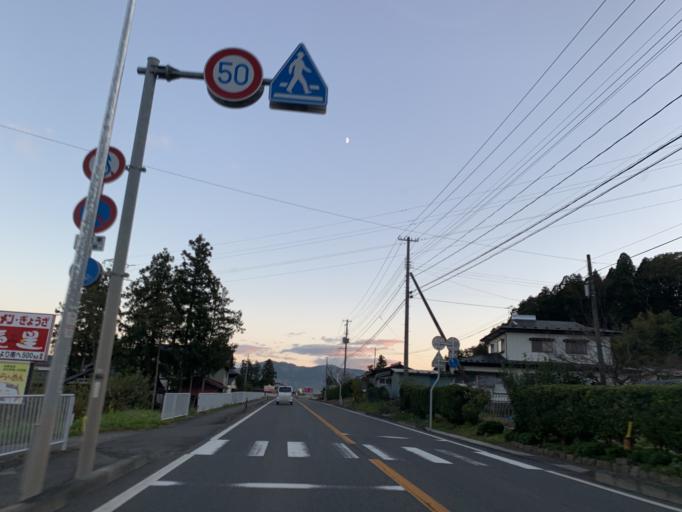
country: JP
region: Iwate
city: Mizusawa
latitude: 39.0901
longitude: 141.1358
